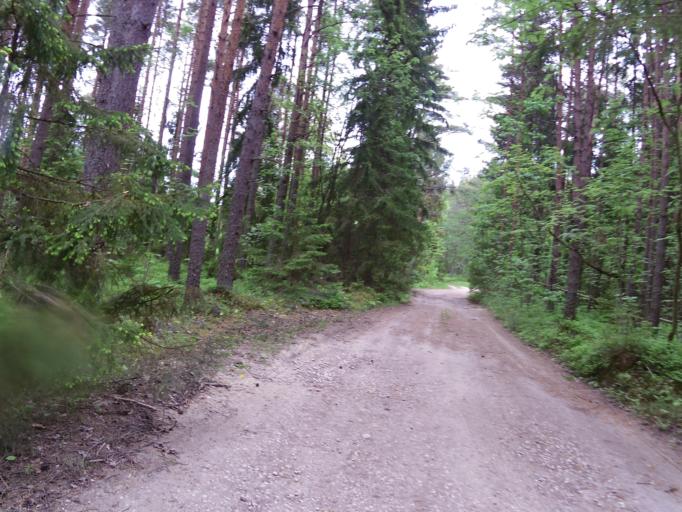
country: EE
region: Harju
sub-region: Paldiski linn
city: Paldiski
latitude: 59.2509
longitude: 23.7495
